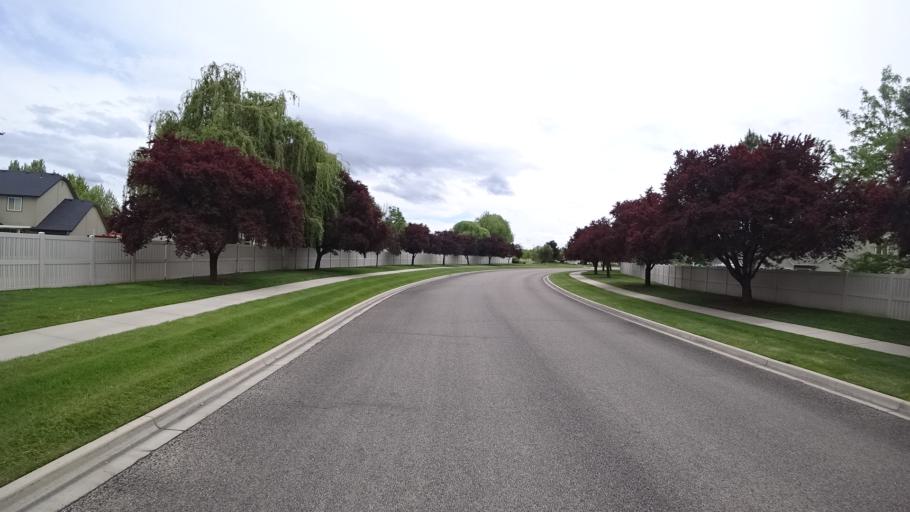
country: US
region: Idaho
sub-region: Ada County
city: Meridian
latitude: 43.6370
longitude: -116.4243
